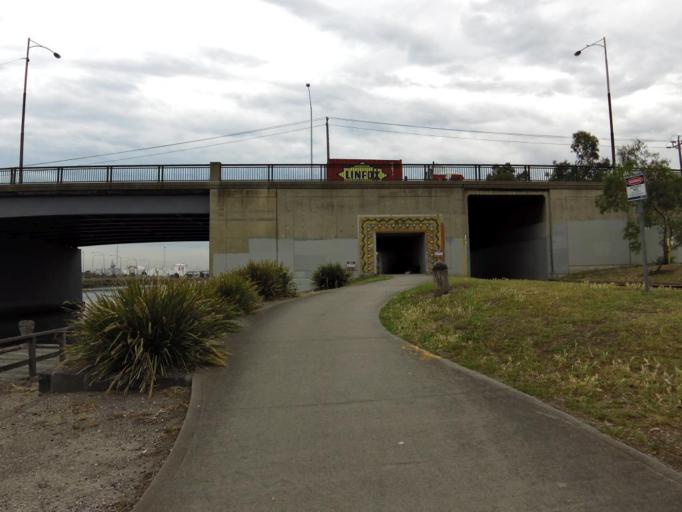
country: AU
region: Victoria
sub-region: Maribyrnong
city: Footscray
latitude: -37.8057
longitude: 144.9073
